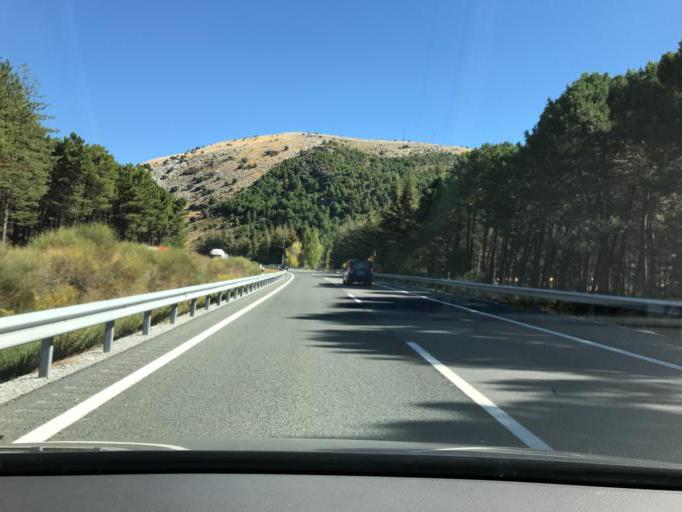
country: ES
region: Andalusia
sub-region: Provincia de Granada
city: Beas de Granada
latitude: 37.2578
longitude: -3.4750
